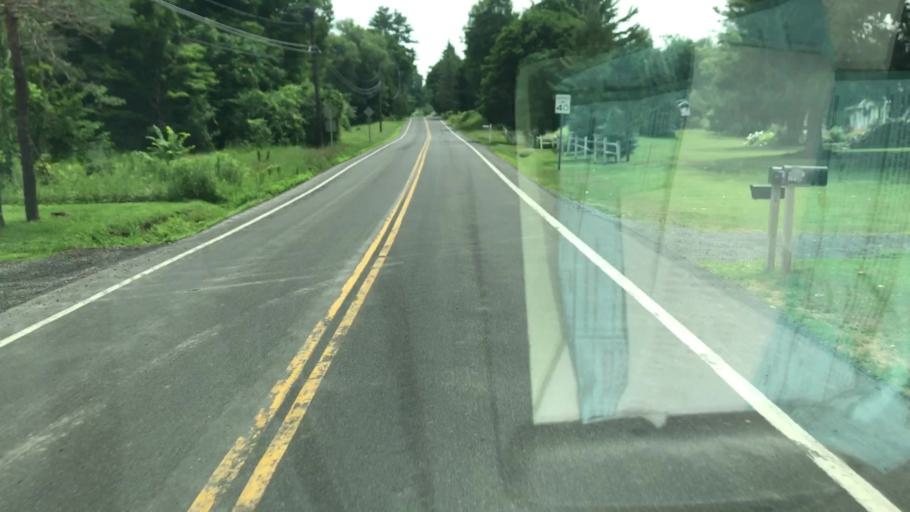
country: US
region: New York
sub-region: Onondaga County
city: Manlius
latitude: 42.9496
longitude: -75.9822
